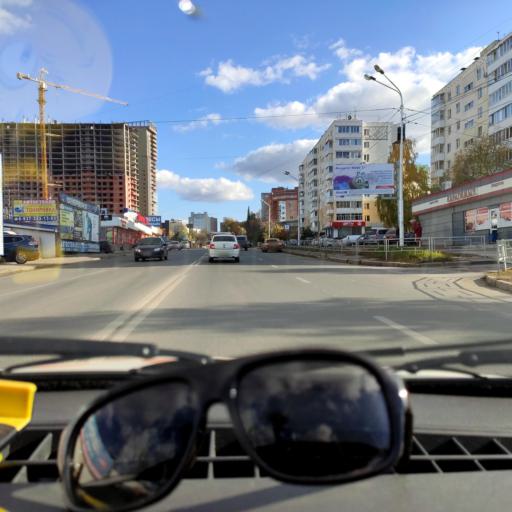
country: RU
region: Bashkortostan
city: Ufa
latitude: 54.7238
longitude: 55.9925
